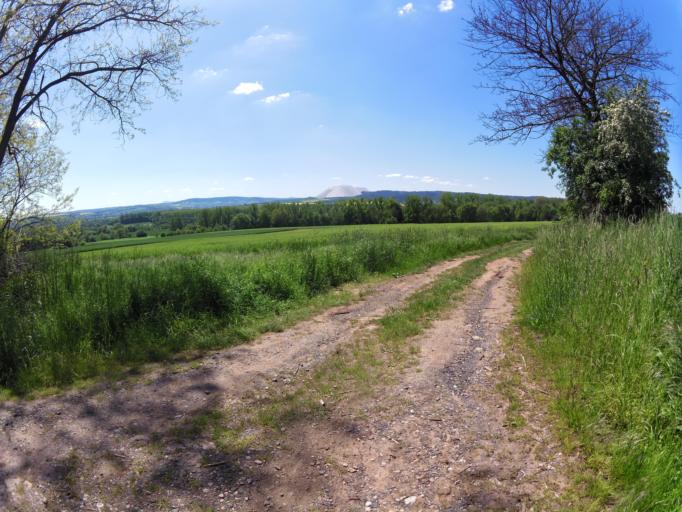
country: DE
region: Thuringia
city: Dankmarshausen
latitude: 50.9574
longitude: 10.0111
